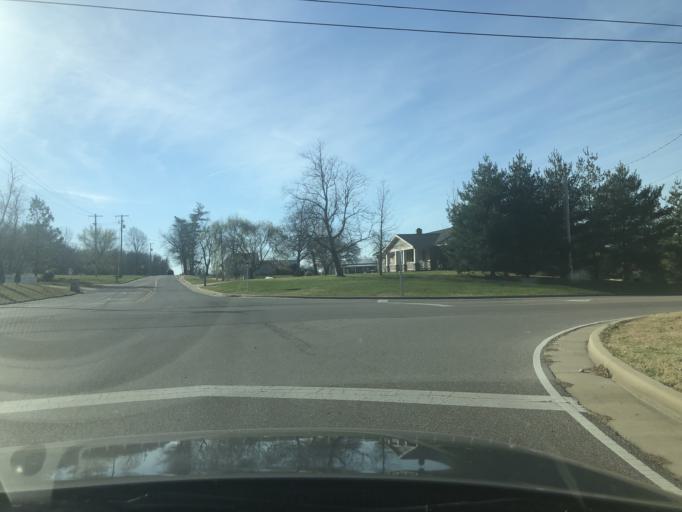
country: US
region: Indiana
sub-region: Warrick County
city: Newburgh
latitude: 37.9913
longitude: -87.4137
